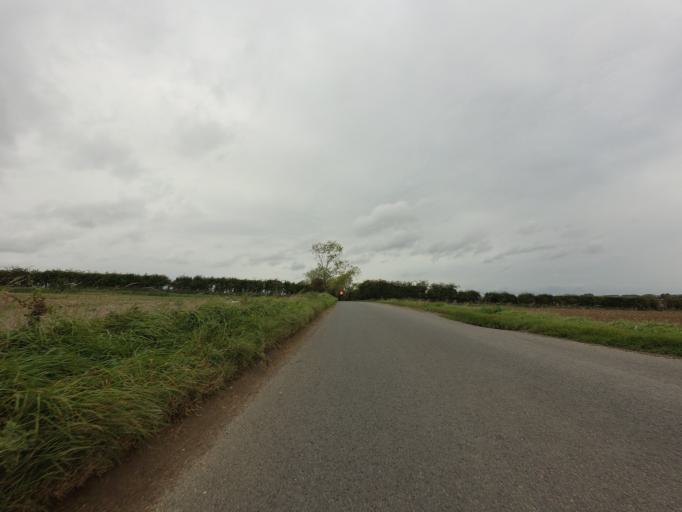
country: GB
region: England
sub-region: Cambridgeshire
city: Duxford
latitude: 52.0443
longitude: 0.1667
